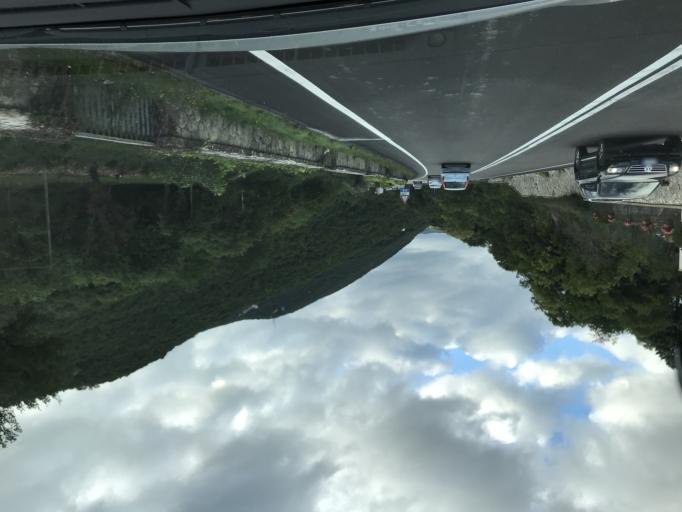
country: IT
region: Umbria
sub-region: Provincia di Perugia
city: Spoleto
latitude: 42.7215
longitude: 12.7309
